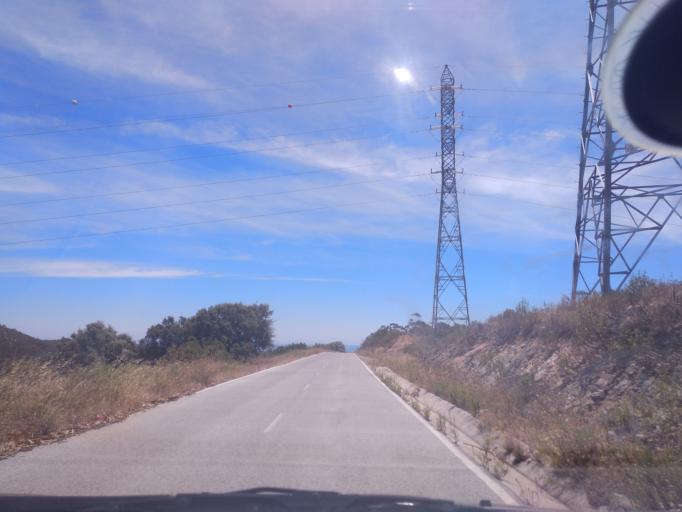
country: PT
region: Faro
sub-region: Sao Bras de Alportel
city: Sao Bras de Alportel
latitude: 37.1964
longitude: -7.8009
